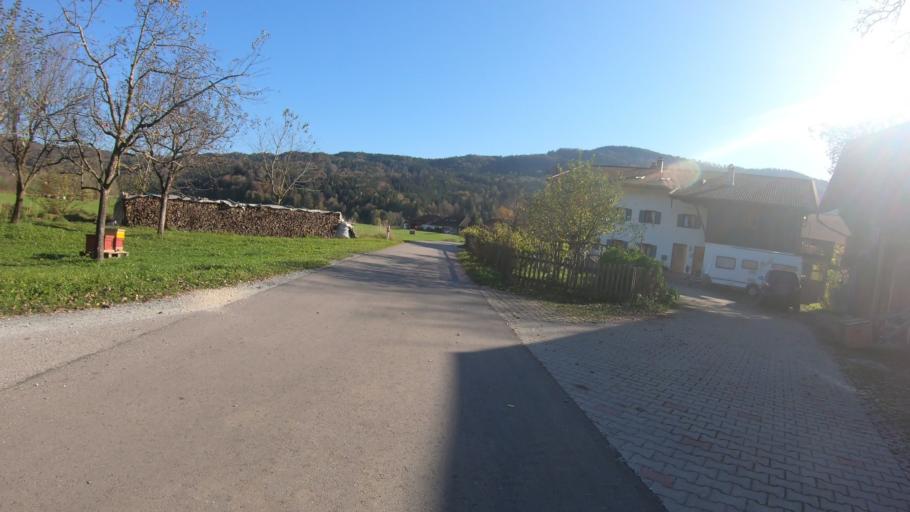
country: DE
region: Bavaria
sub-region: Upper Bavaria
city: Bergen
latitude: 47.8052
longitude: 12.5950
